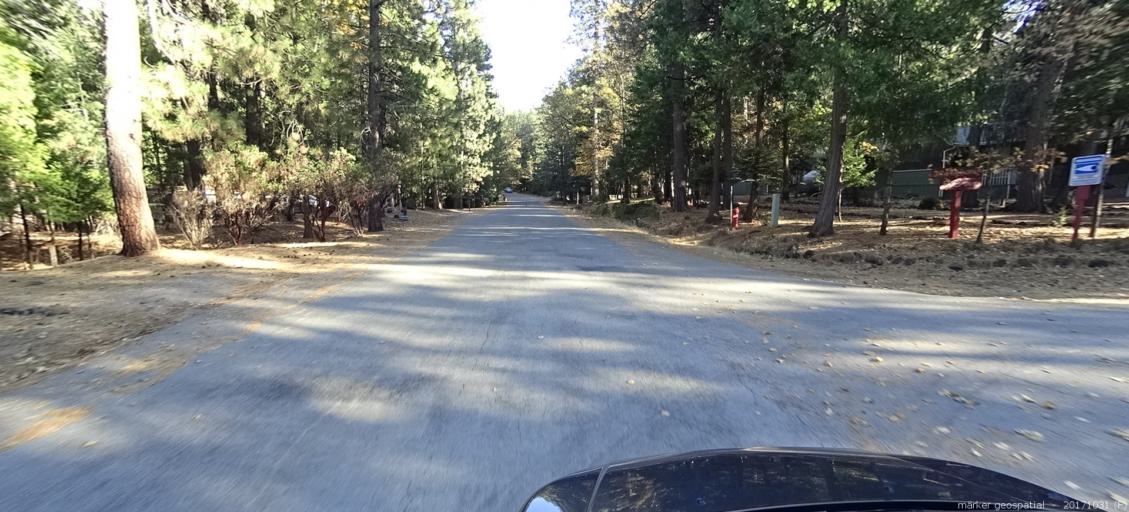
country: US
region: California
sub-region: Shasta County
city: Shingletown
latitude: 40.5000
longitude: -121.9032
